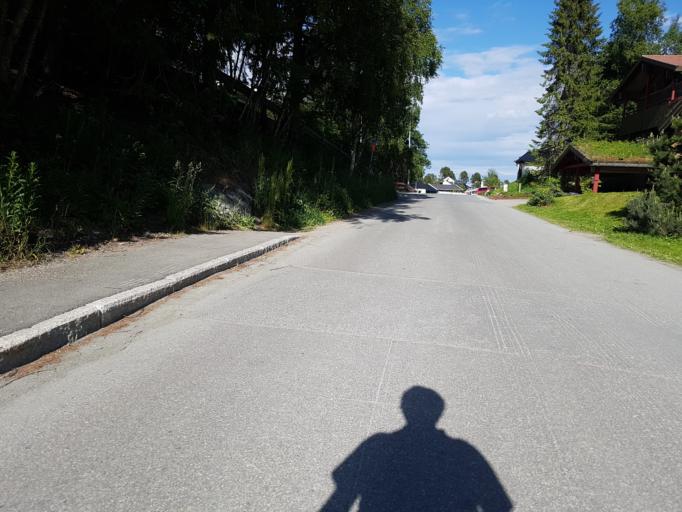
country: NO
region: Sor-Trondelag
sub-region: Trondheim
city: Trondheim
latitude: 63.3968
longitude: 10.3286
